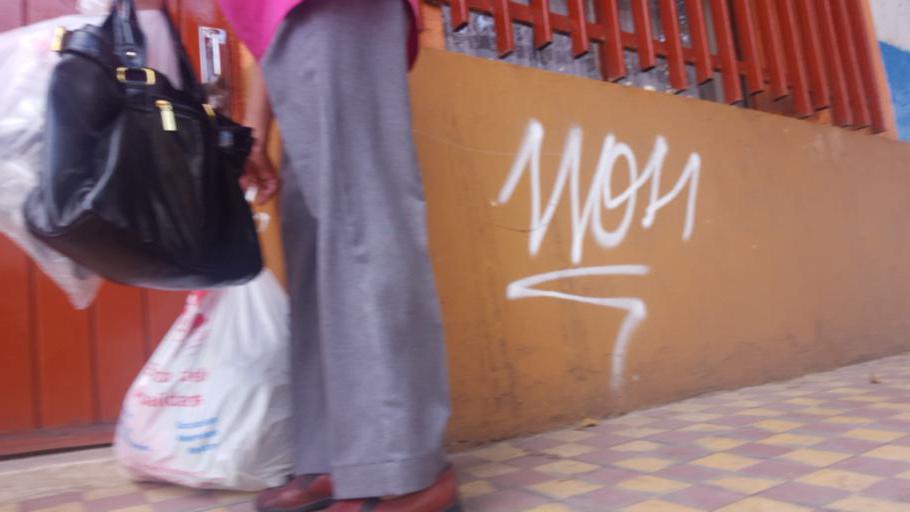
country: MX
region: Jalisco
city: Guadalajara
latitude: 20.6716
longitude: -103.3583
